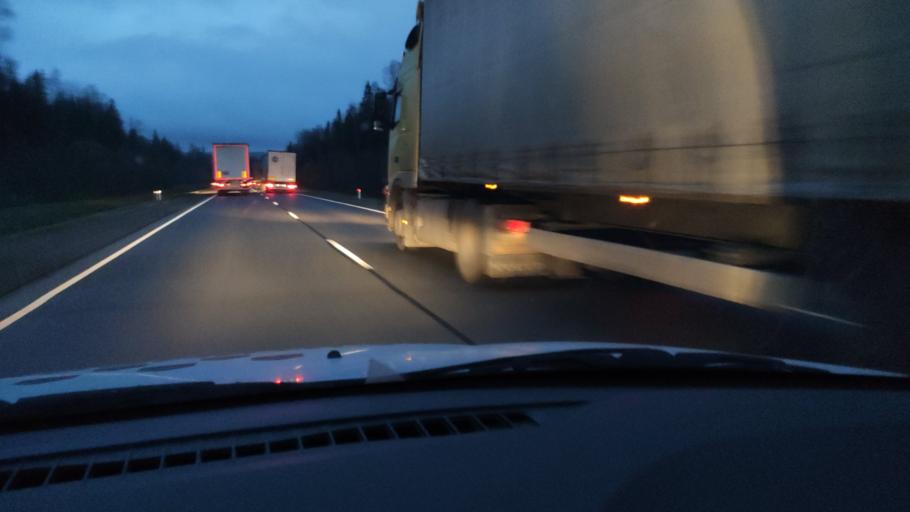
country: RU
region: Kirov
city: Kostino
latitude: 58.8310
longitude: 53.5201
